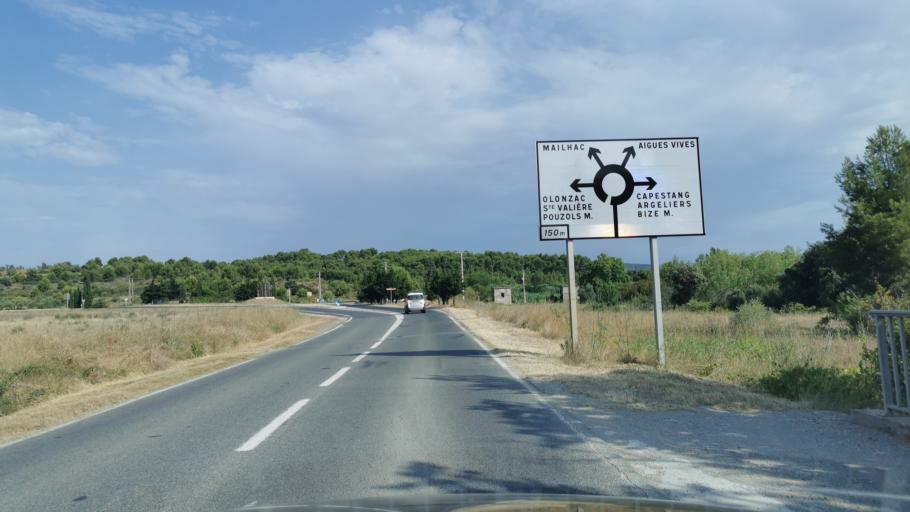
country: FR
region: Languedoc-Roussillon
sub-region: Departement de l'Aude
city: Ginestas
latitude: 43.2901
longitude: 2.8683
